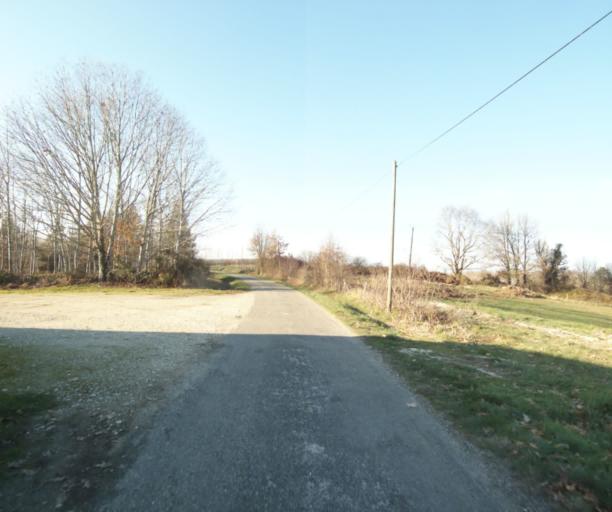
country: FR
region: Midi-Pyrenees
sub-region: Departement du Tarn-et-Garonne
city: Moissac
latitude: 44.1449
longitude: 1.0652
